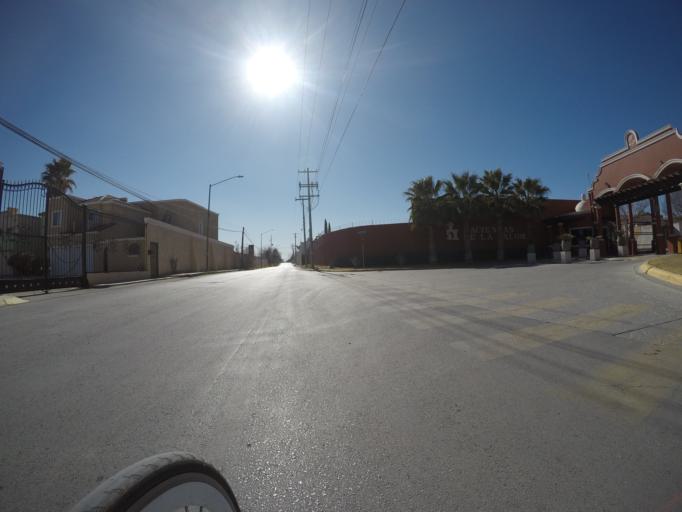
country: US
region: Texas
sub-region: El Paso County
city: Socorro
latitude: 31.6926
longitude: -106.3902
